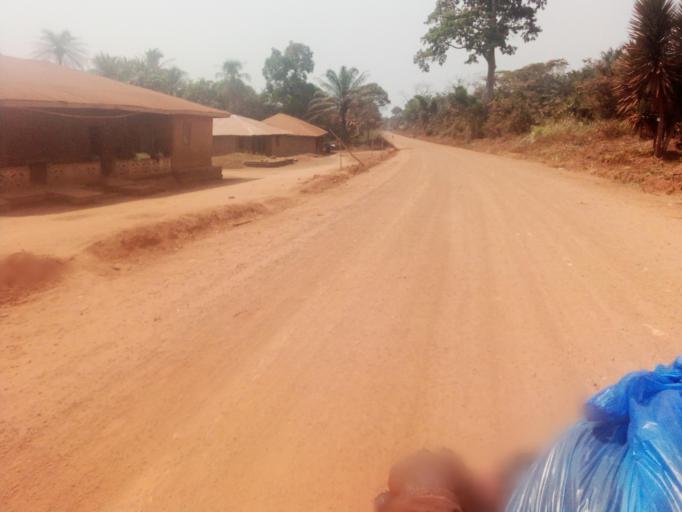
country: SL
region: Southern Province
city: Sumbuya
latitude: 7.6616
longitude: -11.9913
